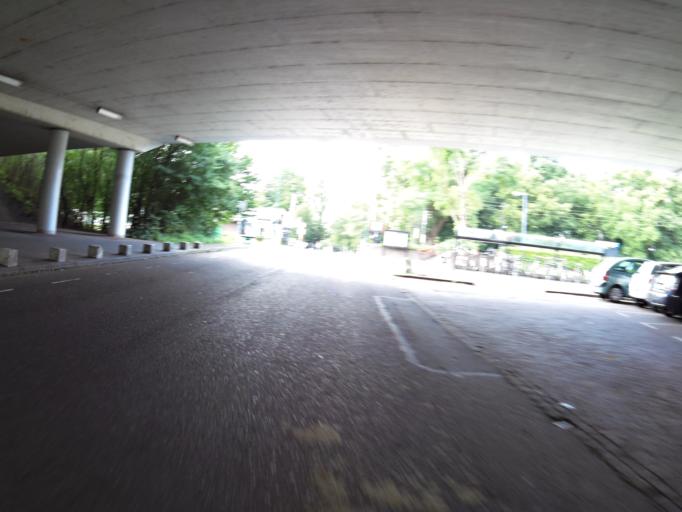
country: NL
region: North Holland
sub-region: Gemeente Hilversum
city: Hilversum
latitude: 52.1782
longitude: 5.1802
